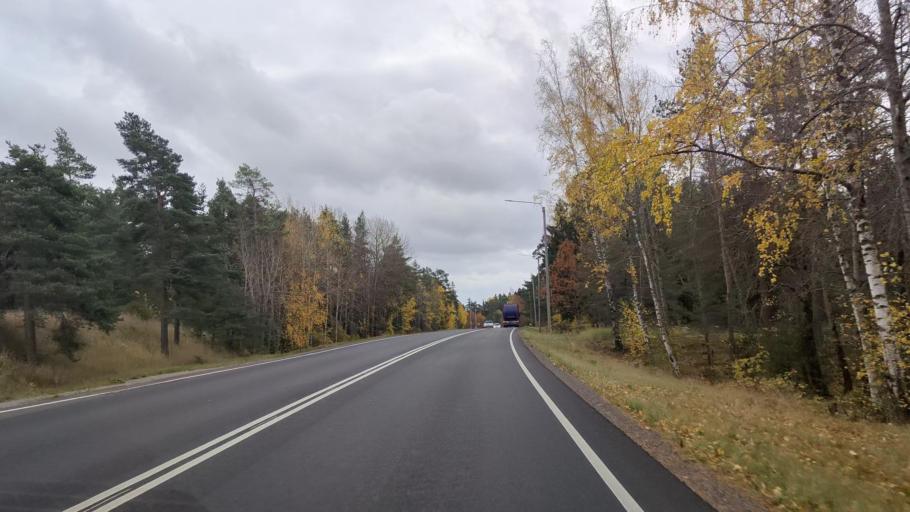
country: FI
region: Varsinais-Suomi
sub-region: Turku
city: Kaarina
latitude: 60.4505
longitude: 22.3726
